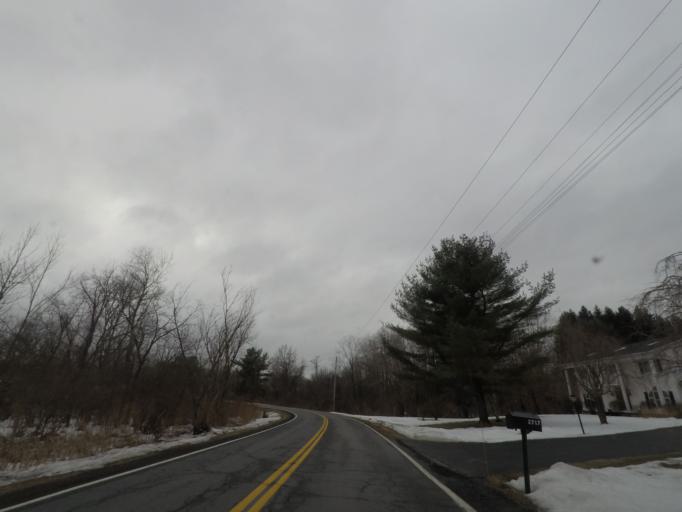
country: US
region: New York
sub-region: Schenectady County
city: Rotterdam
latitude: 42.7429
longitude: -73.9654
